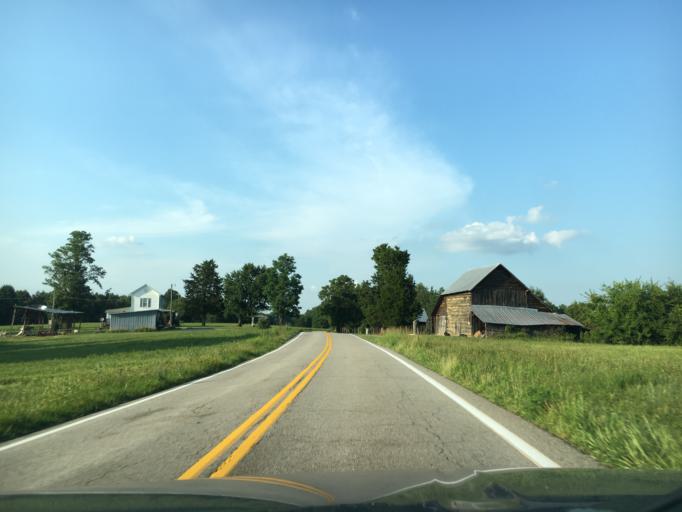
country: US
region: Virginia
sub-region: Pittsylvania County
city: Chatham
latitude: 36.8417
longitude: -79.2225
